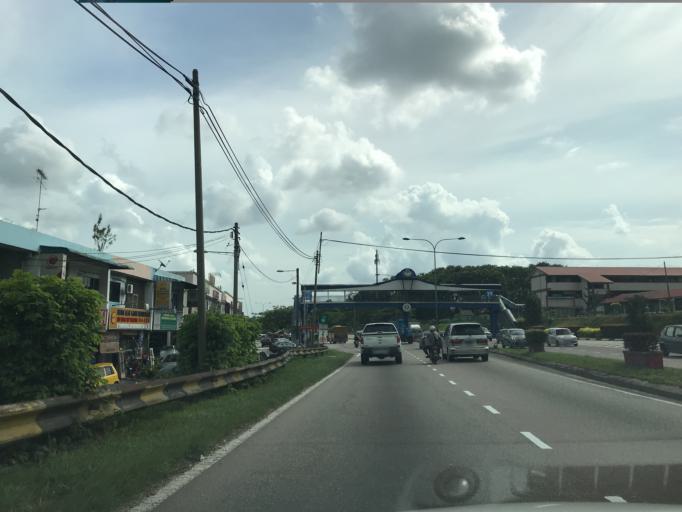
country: MY
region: Johor
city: Taman Senai
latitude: 1.5974
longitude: 103.6456
